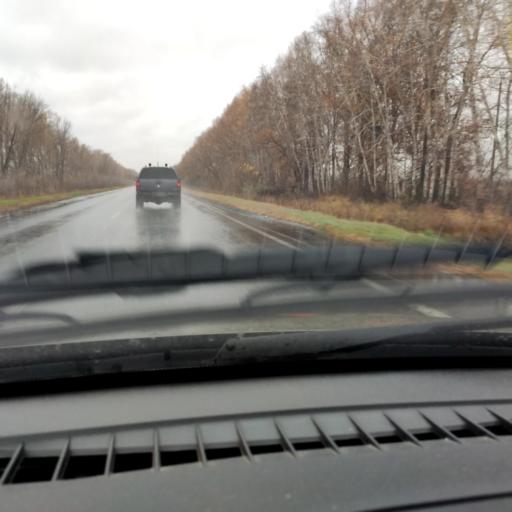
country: RU
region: Samara
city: Tol'yatti
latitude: 53.6030
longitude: 49.3212
